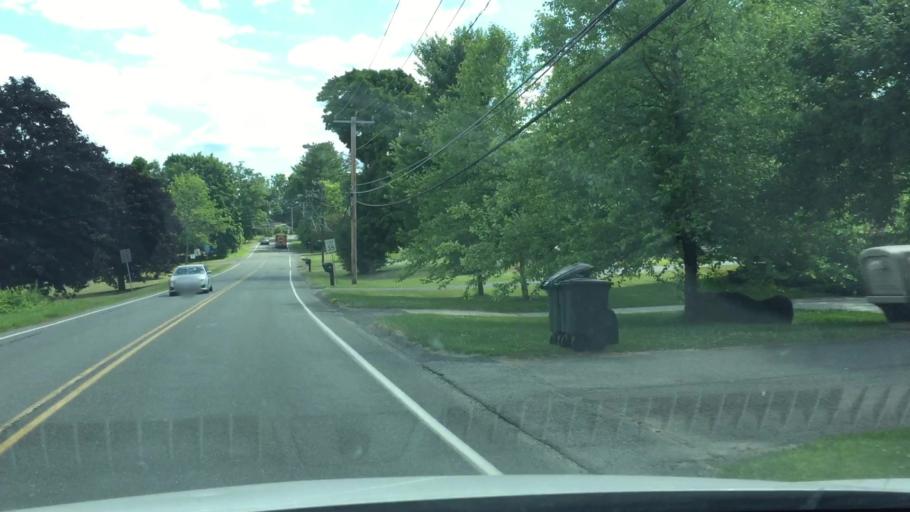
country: US
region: Massachusetts
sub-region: Berkshire County
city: Pittsfield
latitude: 42.4124
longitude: -73.2500
